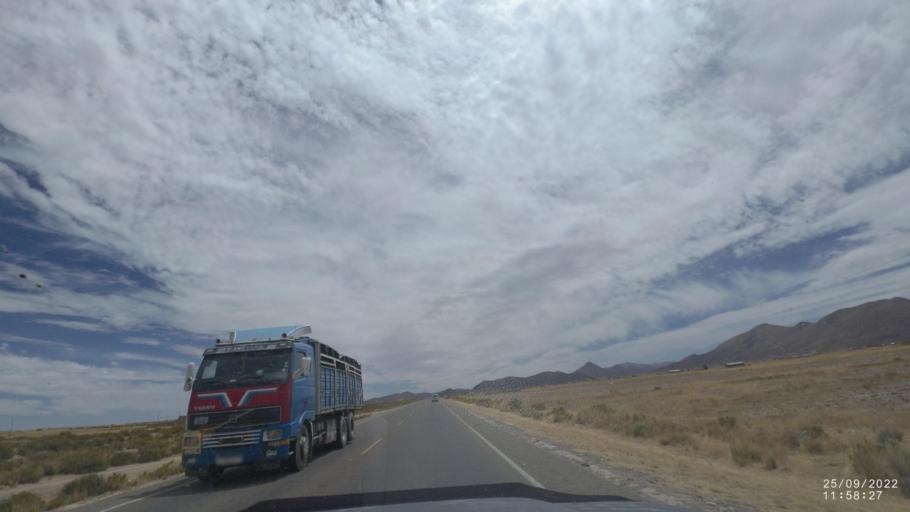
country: BO
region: Oruro
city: Challapata
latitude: -18.8043
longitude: -66.8376
